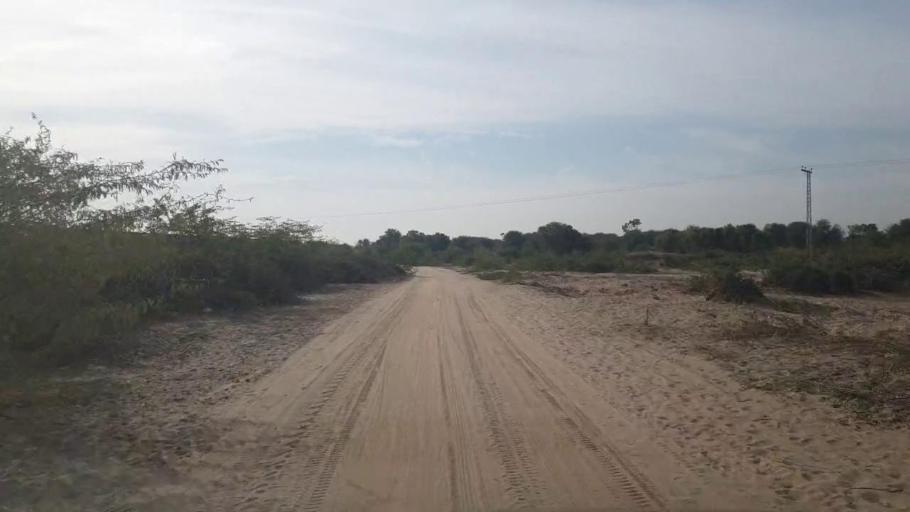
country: PK
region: Sindh
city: Umarkot
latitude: 25.2990
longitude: 69.7187
